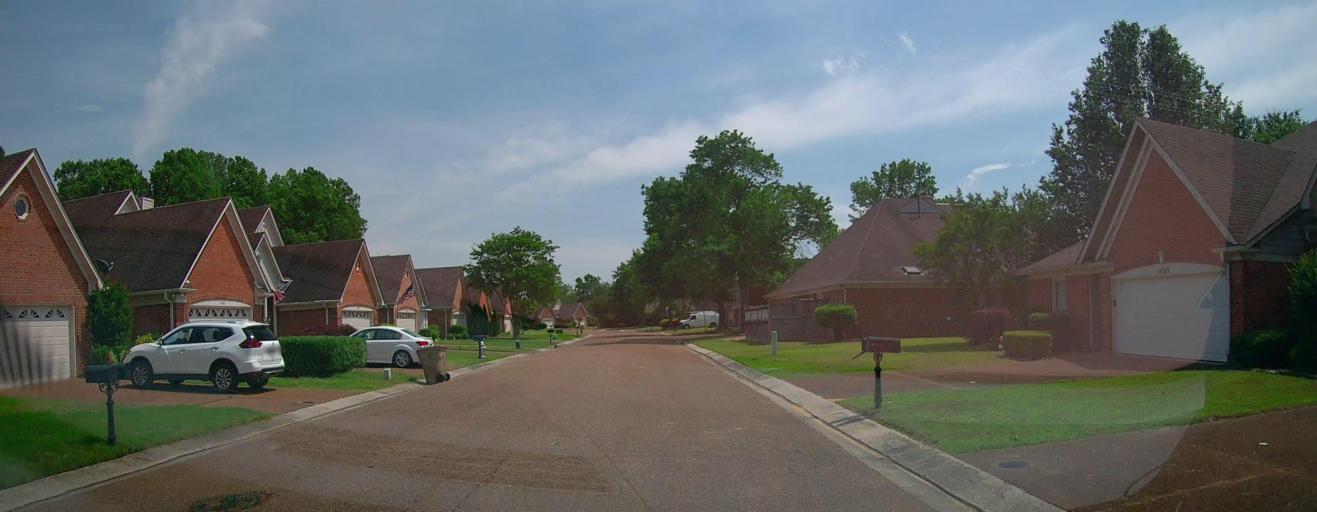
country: US
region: Tennessee
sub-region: Shelby County
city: Germantown
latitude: 35.0398
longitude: -89.7847
